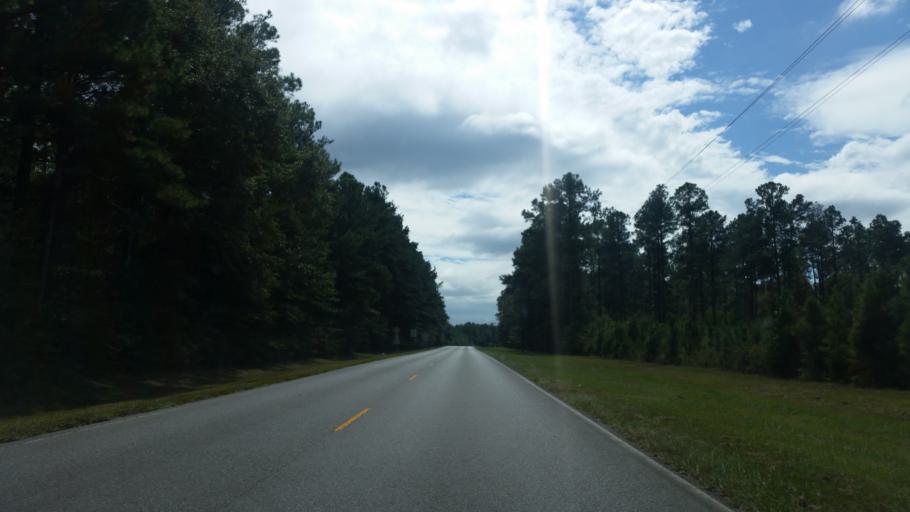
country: US
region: Florida
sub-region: Santa Rosa County
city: Point Baker
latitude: 30.7544
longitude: -86.9431
